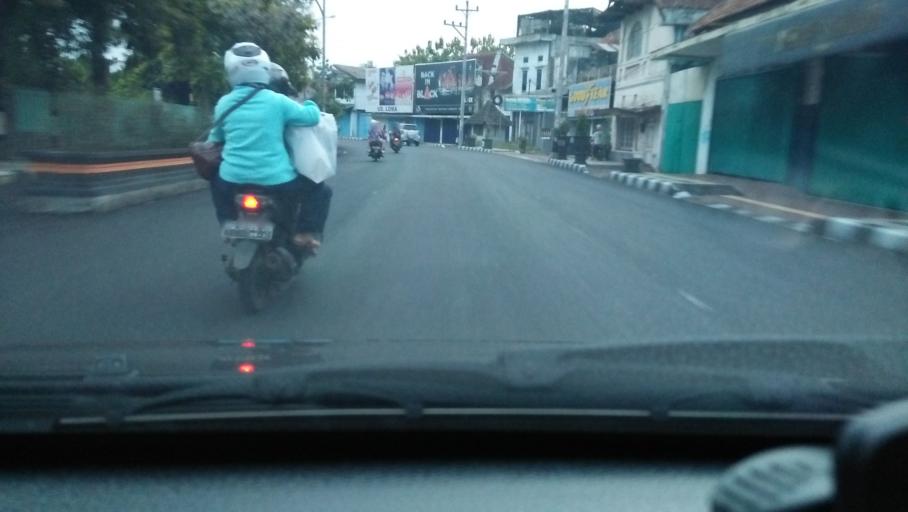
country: ID
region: Central Java
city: Magelang
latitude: -7.4695
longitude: 110.2183
